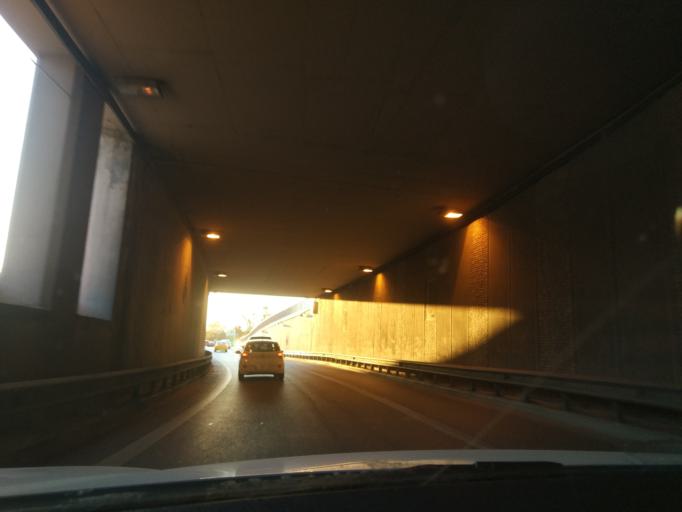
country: TR
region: Istanbul
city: UEskuedar
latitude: 41.0241
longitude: 29.0571
